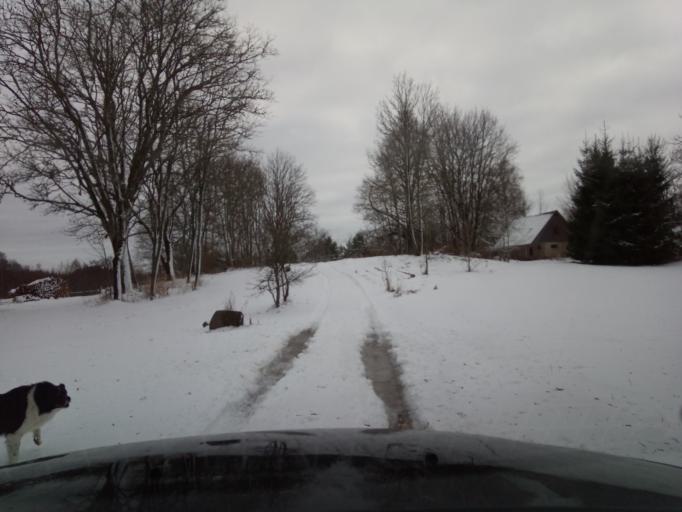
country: LT
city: Zarasai
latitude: 55.6739
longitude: 25.9800
